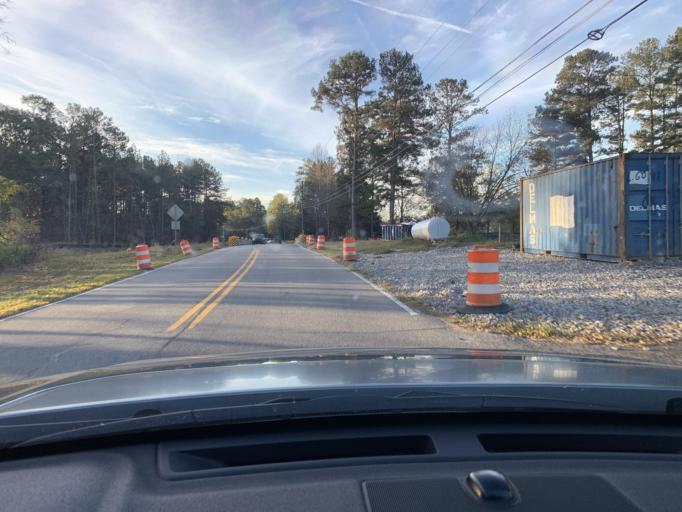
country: US
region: Georgia
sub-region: Clarke County
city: Country Club Estates
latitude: 33.9373
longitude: -83.4615
